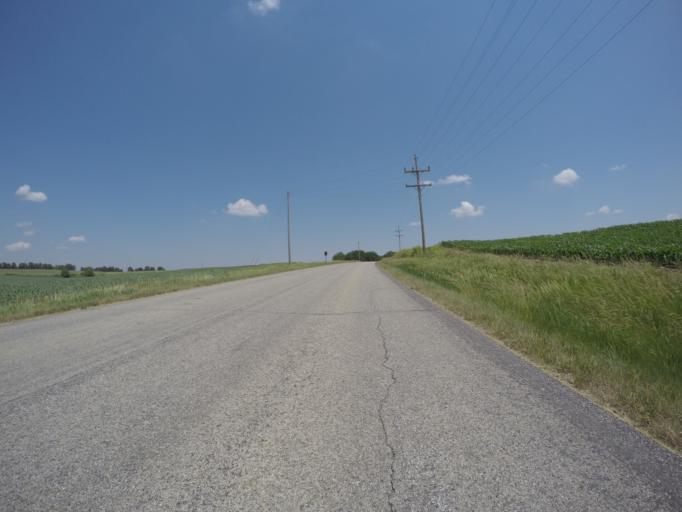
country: US
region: Kansas
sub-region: Doniphan County
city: Troy
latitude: 39.7670
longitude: -95.1271
